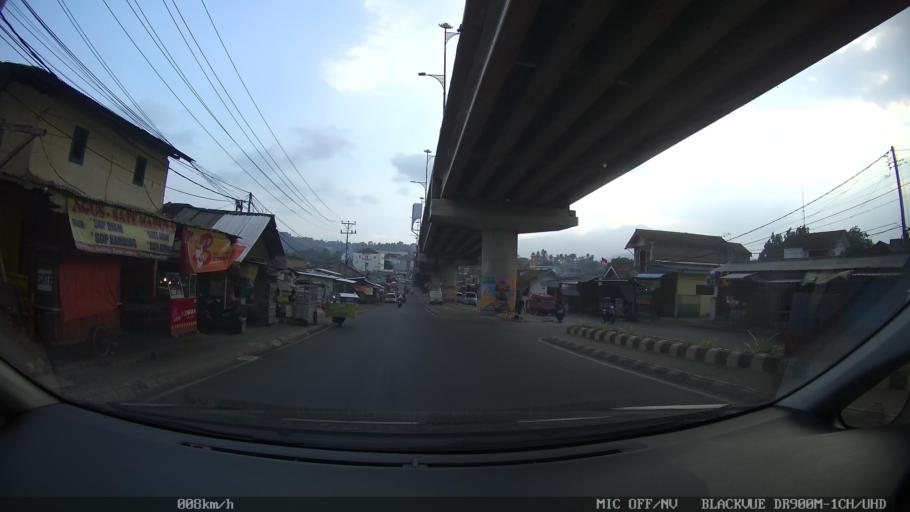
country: ID
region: Lampung
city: Kedaton
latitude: -5.3929
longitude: 105.2156
